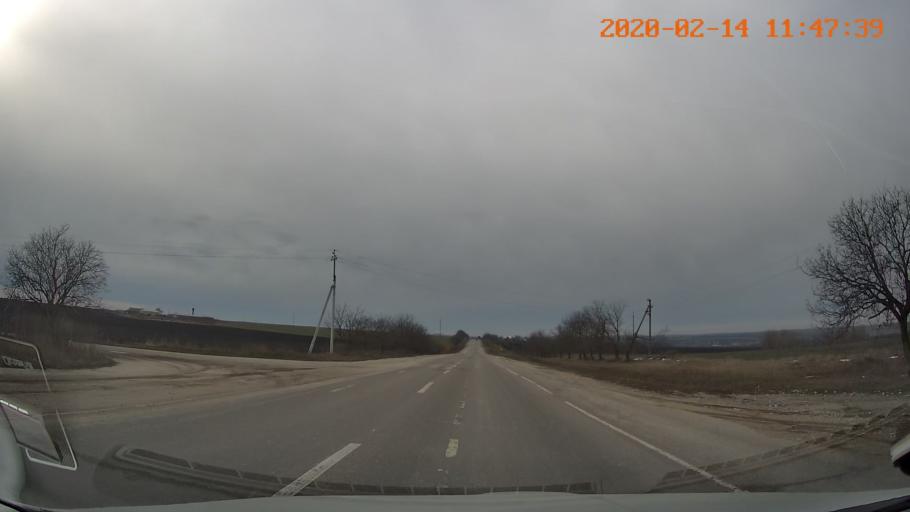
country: MD
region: Briceni
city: Briceni
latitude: 48.3146
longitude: 26.9657
